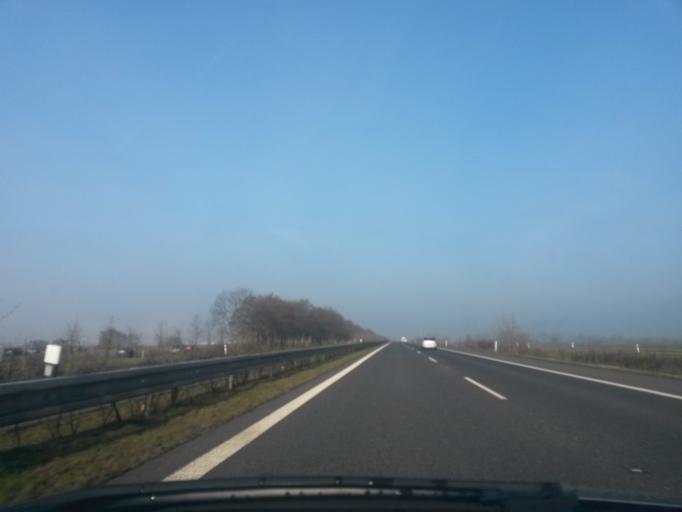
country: CZ
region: Ustecky
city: Zatec
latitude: 50.3733
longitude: 13.6088
